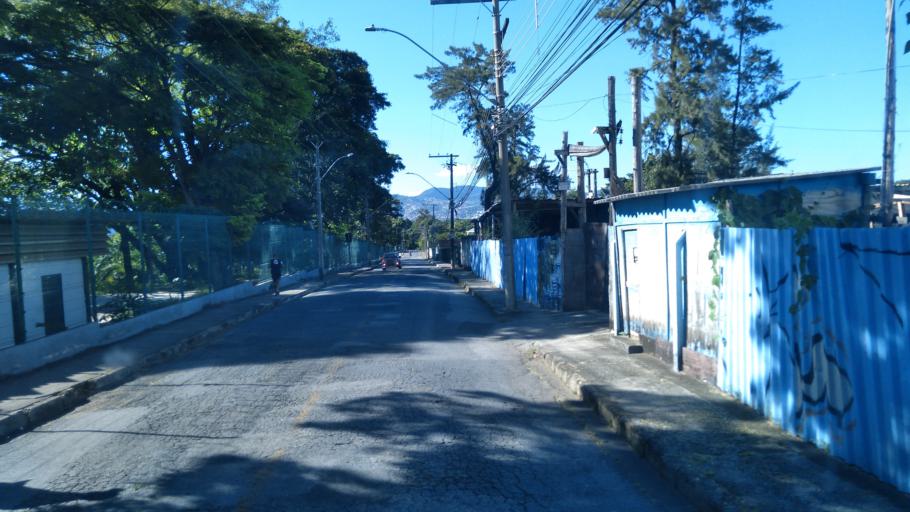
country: BR
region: Minas Gerais
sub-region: Belo Horizonte
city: Belo Horizonte
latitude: -19.8846
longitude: -43.9150
